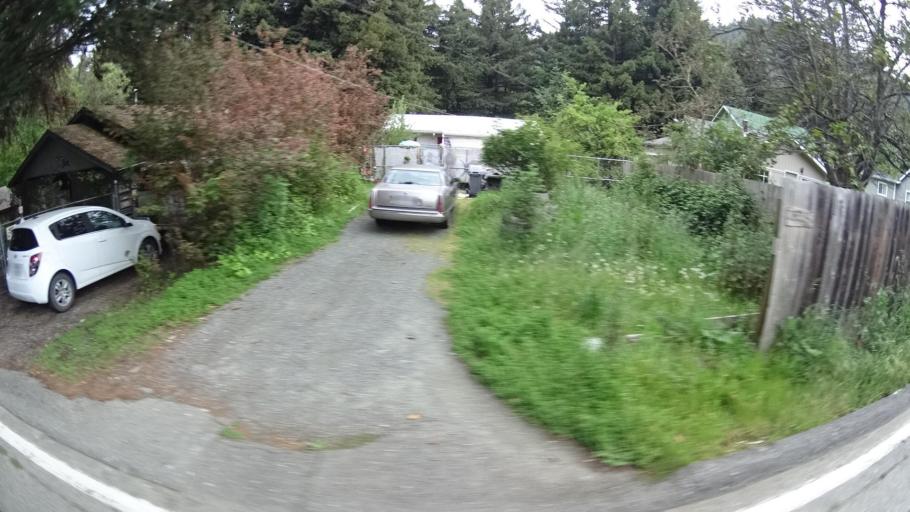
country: US
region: California
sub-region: Humboldt County
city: Redway
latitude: 40.3217
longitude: -123.9235
